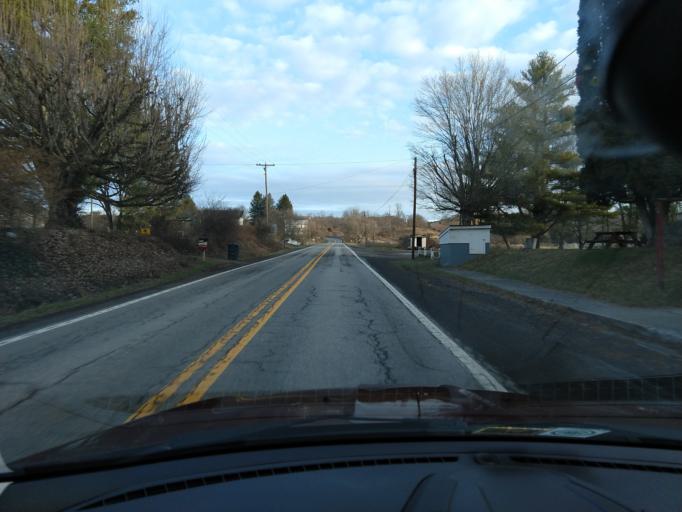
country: US
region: West Virginia
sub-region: Greenbrier County
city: White Sulphur Springs
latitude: 37.9962
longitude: -80.3628
